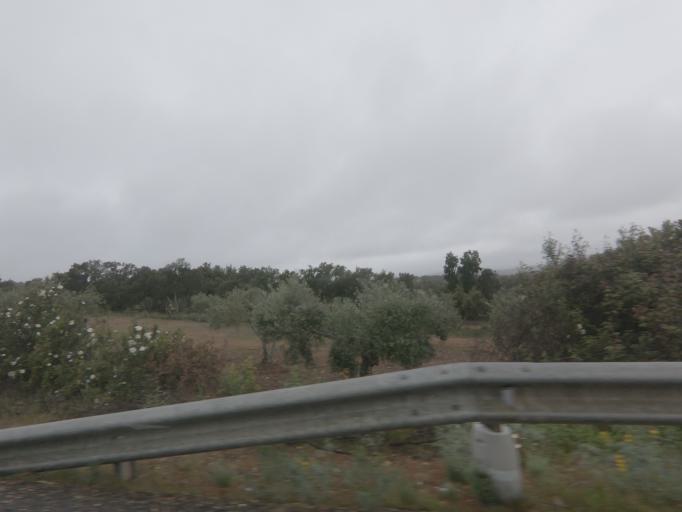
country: ES
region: Extremadura
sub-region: Provincia de Badajoz
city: Puebla de Obando
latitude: 39.1680
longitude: -6.6310
